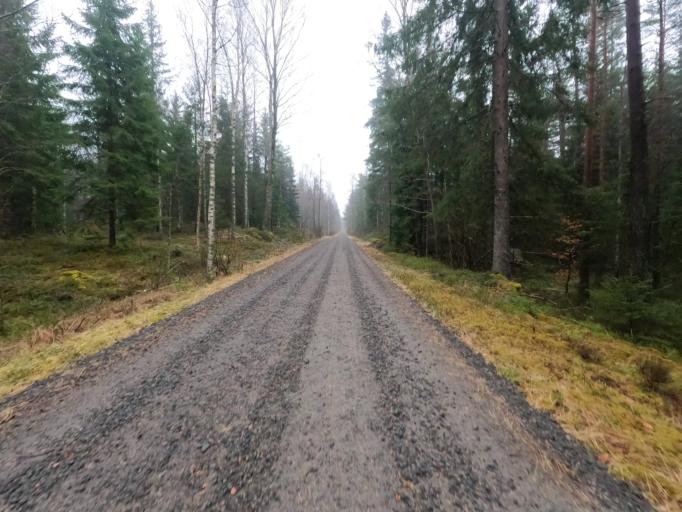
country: SE
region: Halland
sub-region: Hylte Kommun
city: Hyltebruk
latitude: 56.8139
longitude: 13.3163
